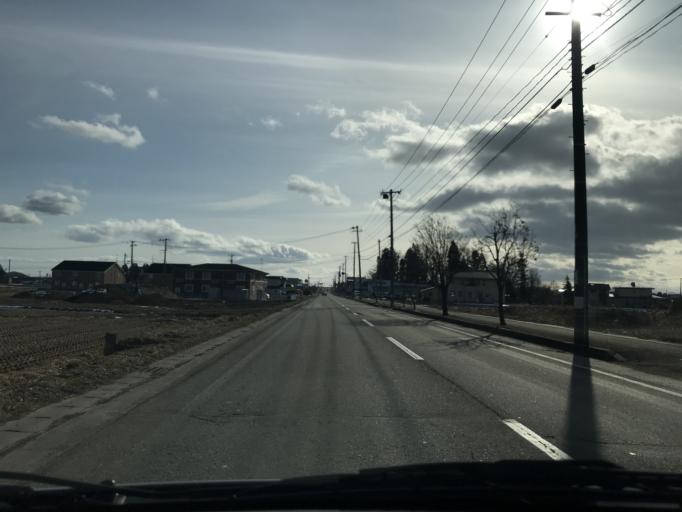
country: JP
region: Iwate
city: Kitakami
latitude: 39.3017
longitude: 141.0985
